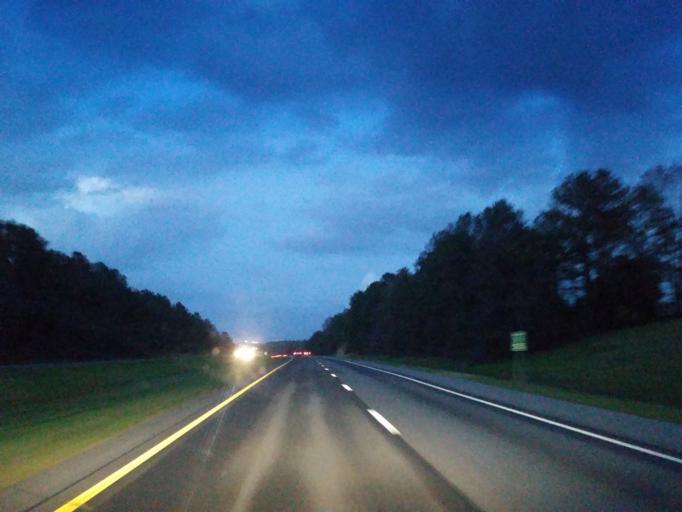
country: US
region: Alabama
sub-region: Sumter County
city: Livingston
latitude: 32.5983
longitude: -88.2223
